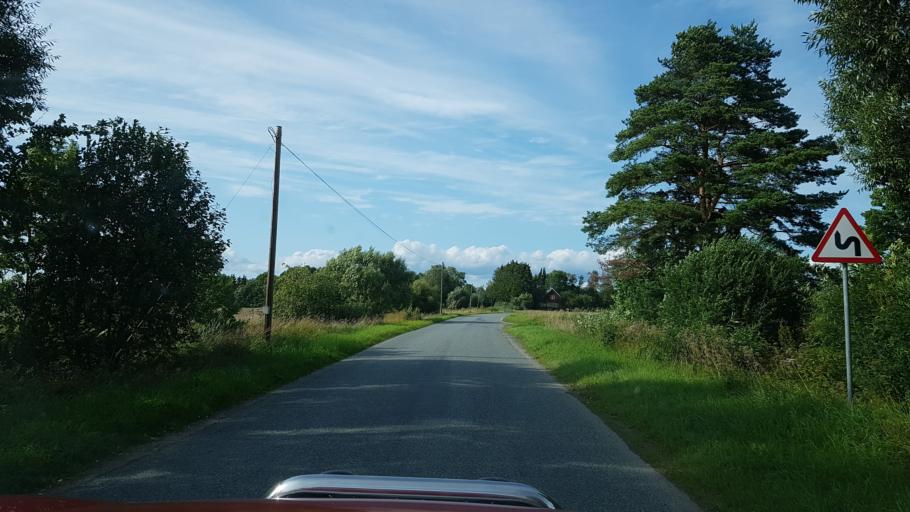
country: EE
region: Laeaene
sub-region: Lihula vald
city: Lihula
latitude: 58.4412
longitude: 24.0038
